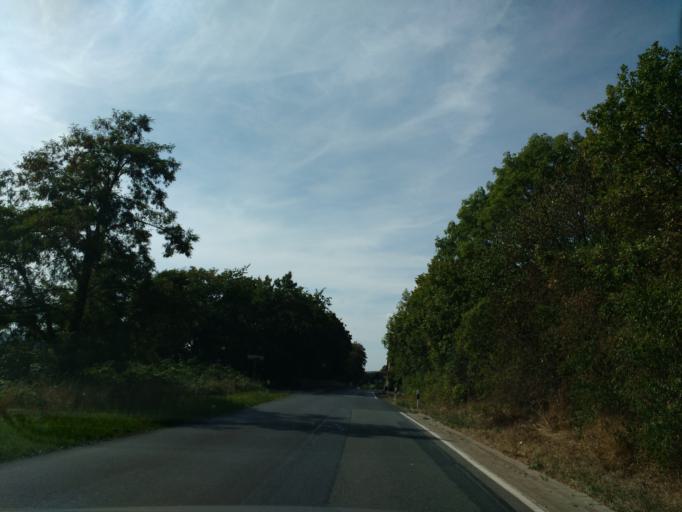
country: DE
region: Lower Saxony
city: Hameln
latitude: 52.0478
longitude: 9.4049
